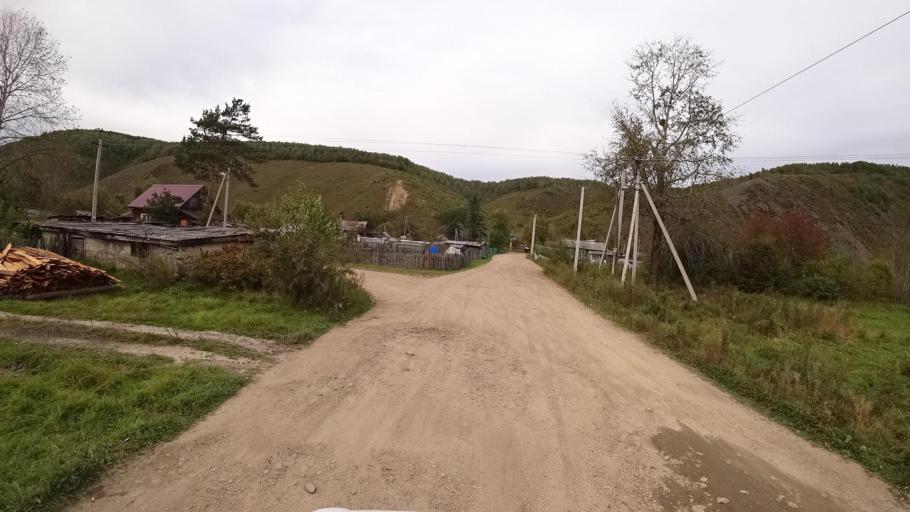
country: RU
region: Jewish Autonomous Oblast
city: Khingansk
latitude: 49.1275
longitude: 131.1877
